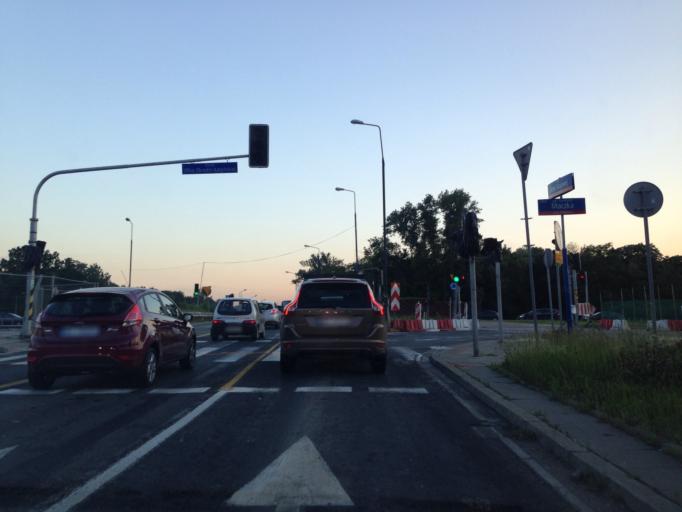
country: PL
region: Masovian Voivodeship
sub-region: Warszawa
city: Zoliborz
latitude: 52.2629
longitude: 20.9533
